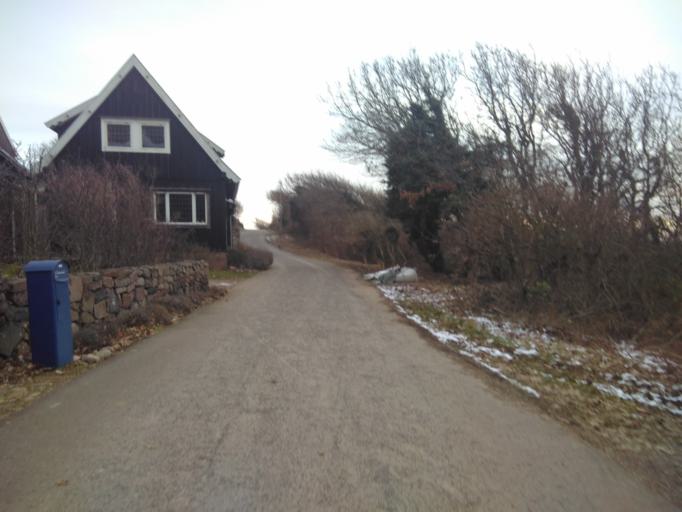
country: SE
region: Skane
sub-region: Hoganas Kommun
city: Hoganas
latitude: 56.2889
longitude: 12.4869
